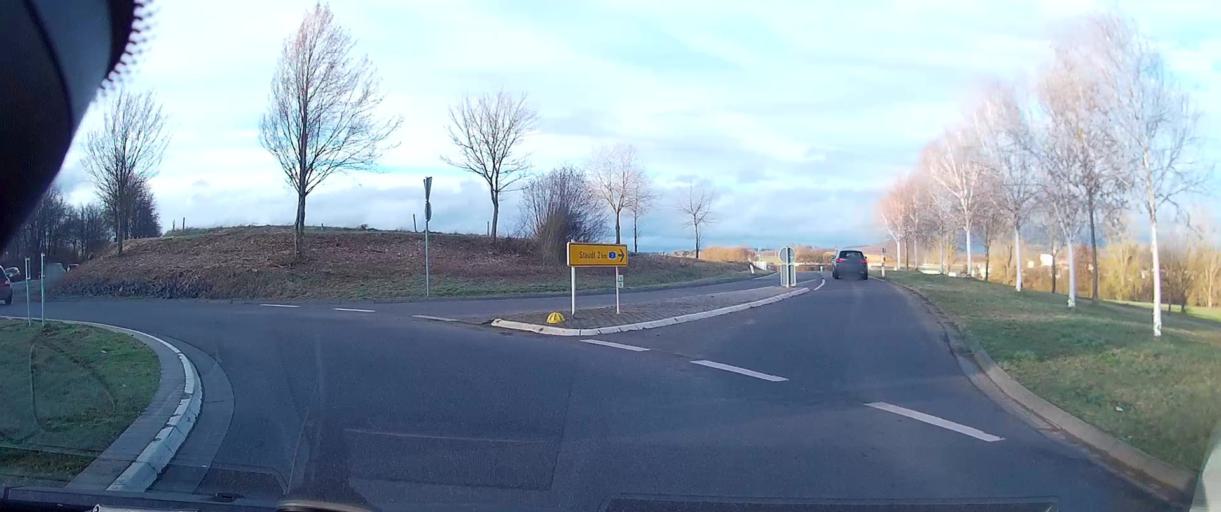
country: DE
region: Rheinland-Pfalz
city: Wirges
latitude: 50.4580
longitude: 7.8055
